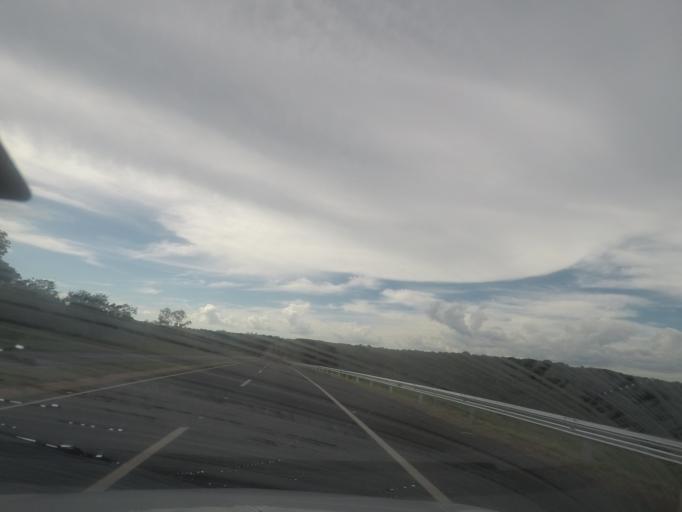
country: BR
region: Minas Gerais
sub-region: Prata
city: Prata
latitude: -19.4185
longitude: -48.8899
